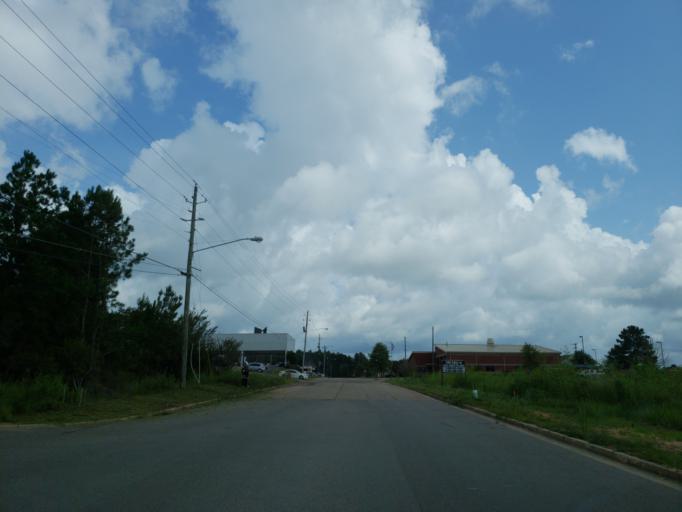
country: US
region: Mississippi
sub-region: Lamar County
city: West Hattiesburg
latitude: 31.3166
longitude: -89.3939
